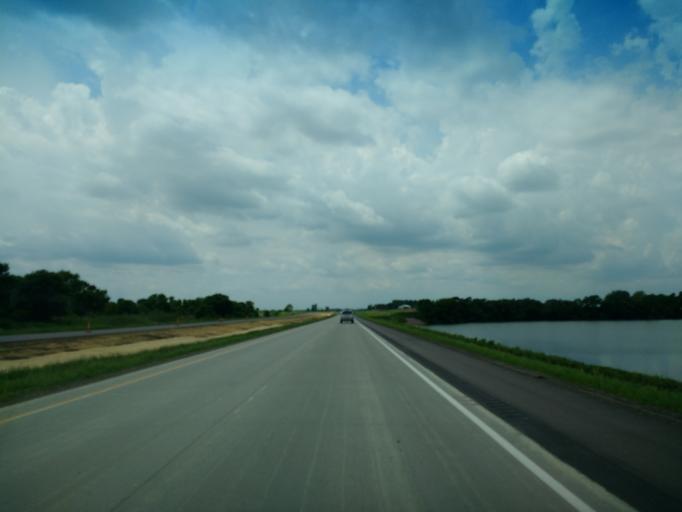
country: US
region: Minnesota
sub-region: Cottonwood County
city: Windom
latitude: 43.8983
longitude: -95.0728
